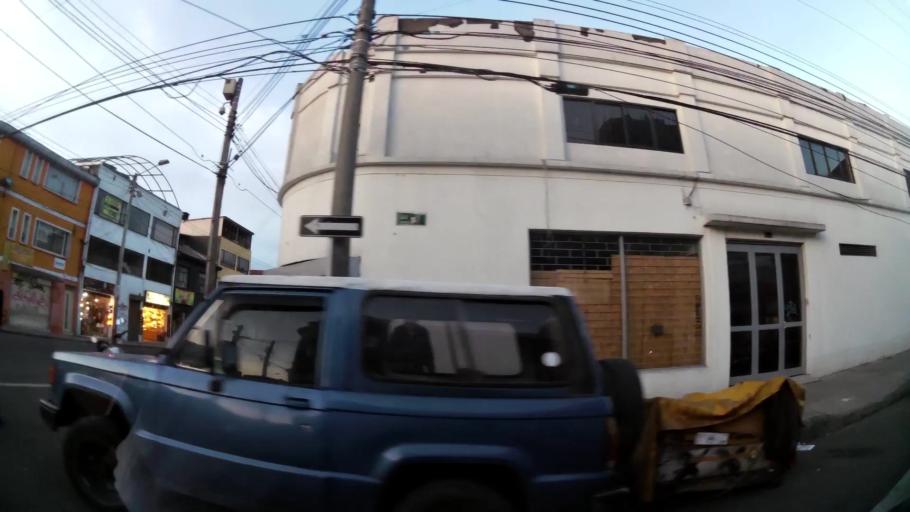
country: CO
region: Bogota D.C.
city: Barrio San Luis
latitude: 4.6581
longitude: -74.0645
